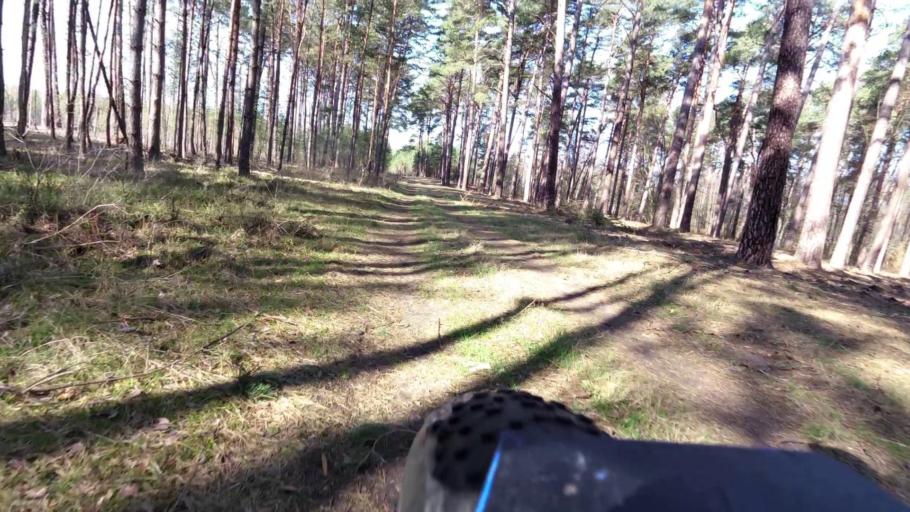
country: PL
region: Lubusz
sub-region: Powiat krosnienski
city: Maszewo
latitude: 52.2100
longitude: 14.9518
